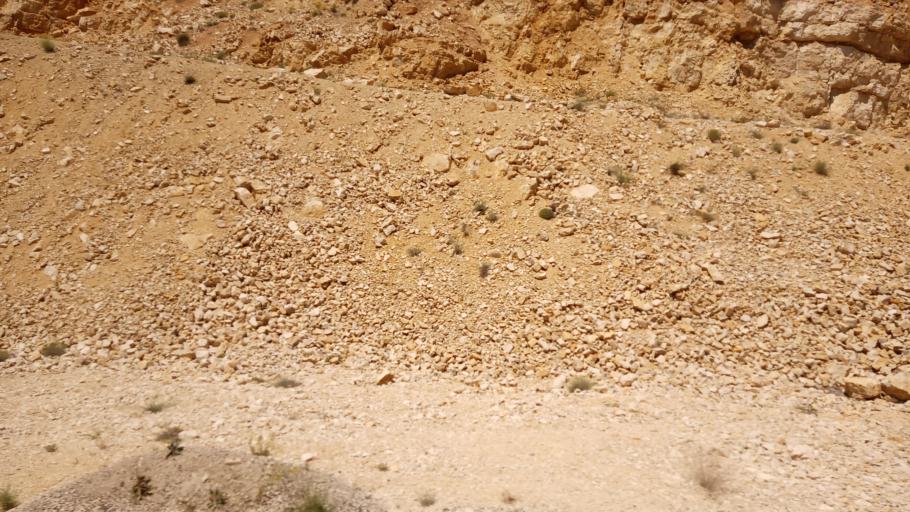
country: TR
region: Malatya
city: Darende
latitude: 38.6269
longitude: 37.4569
